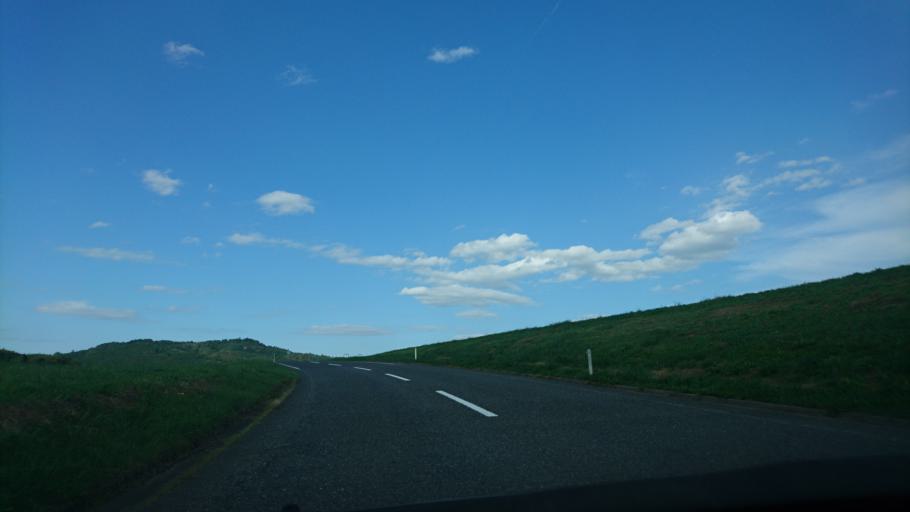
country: JP
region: Iwate
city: Ichinoseki
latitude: 38.8322
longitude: 141.2585
